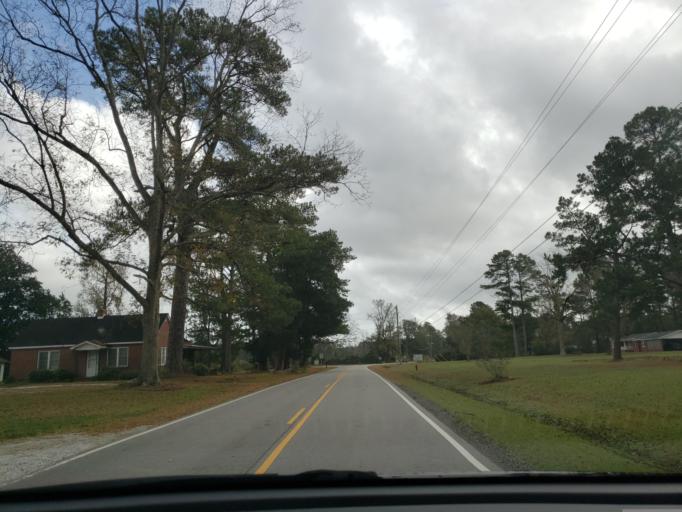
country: US
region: North Carolina
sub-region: Onslow County
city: Jacksonville
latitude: 34.7216
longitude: -77.5792
